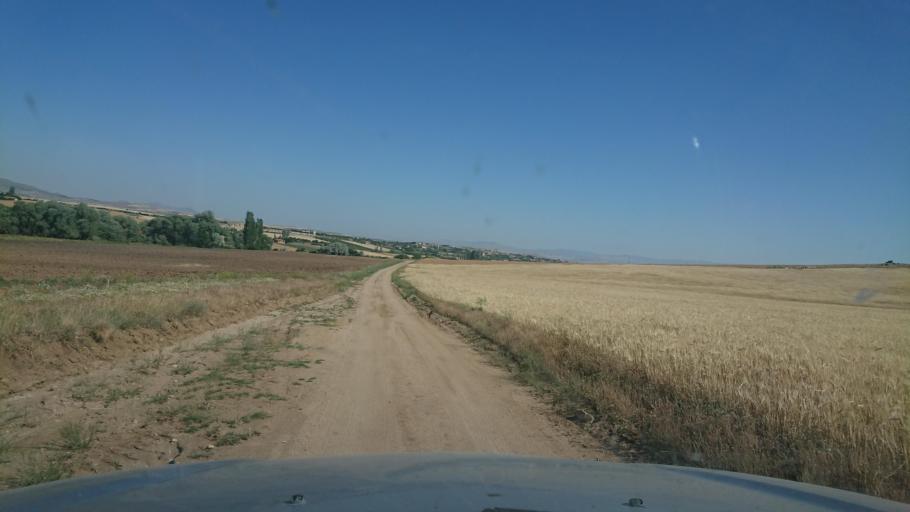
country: TR
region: Aksaray
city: Agacoren
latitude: 38.8504
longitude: 33.9156
